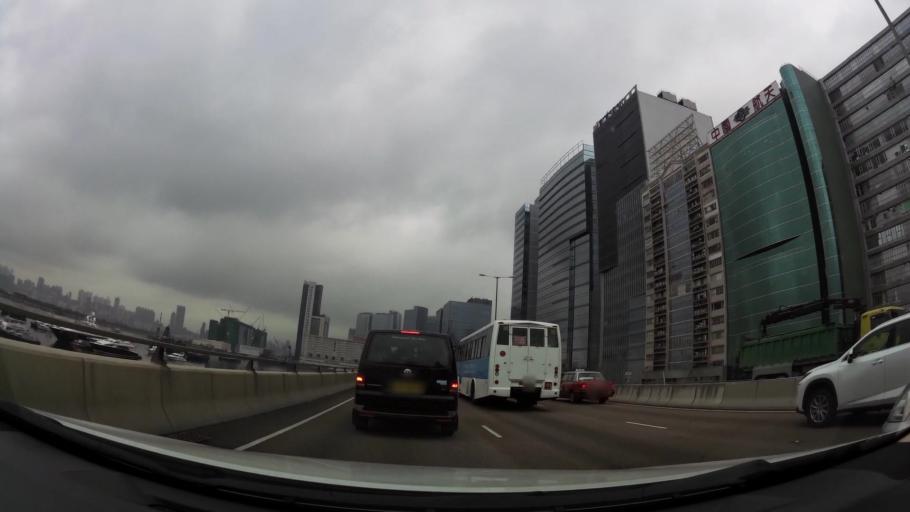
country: HK
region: Kowloon City
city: Kowloon
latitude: 22.3108
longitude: 114.2176
